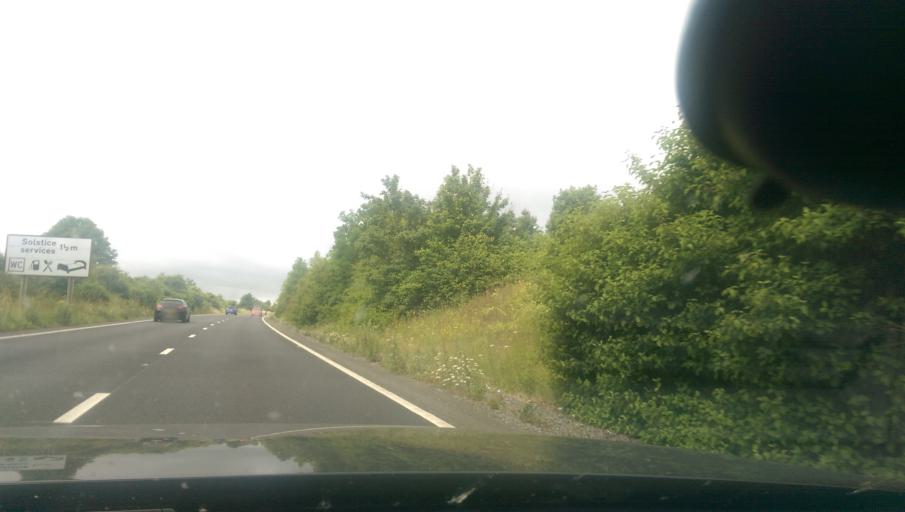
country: GB
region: England
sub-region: Wiltshire
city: Allington
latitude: 51.1812
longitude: -1.7142
